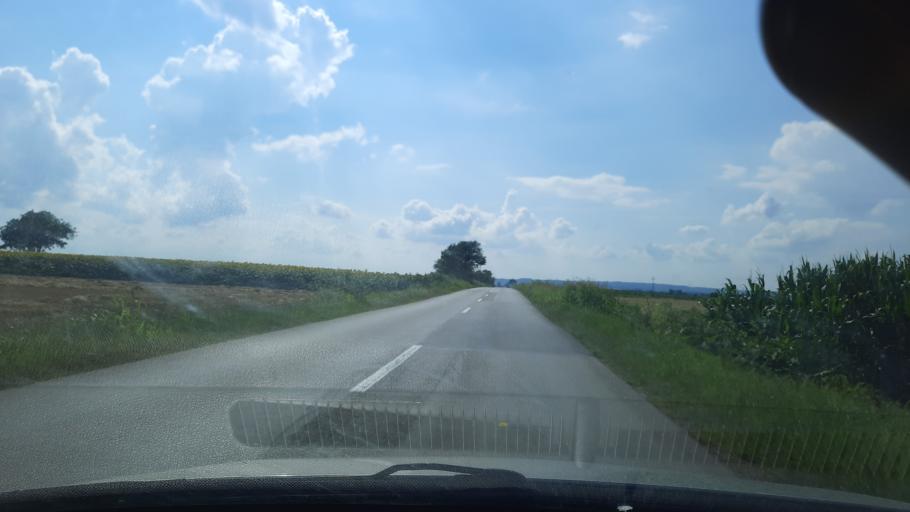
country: RS
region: Central Serbia
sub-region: Branicevski Okrug
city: Malo Crnice
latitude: 44.5819
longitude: 21.3104
